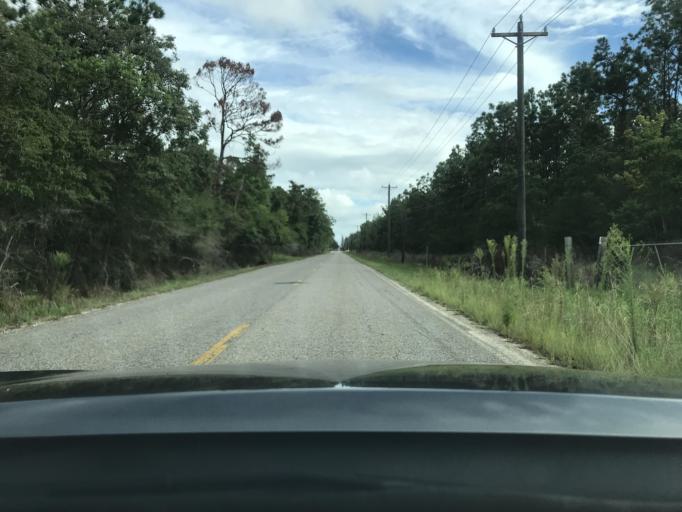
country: US
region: Louisiana
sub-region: Calcasieu Parish
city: Westlake
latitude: 30.2682
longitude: -93.2751
